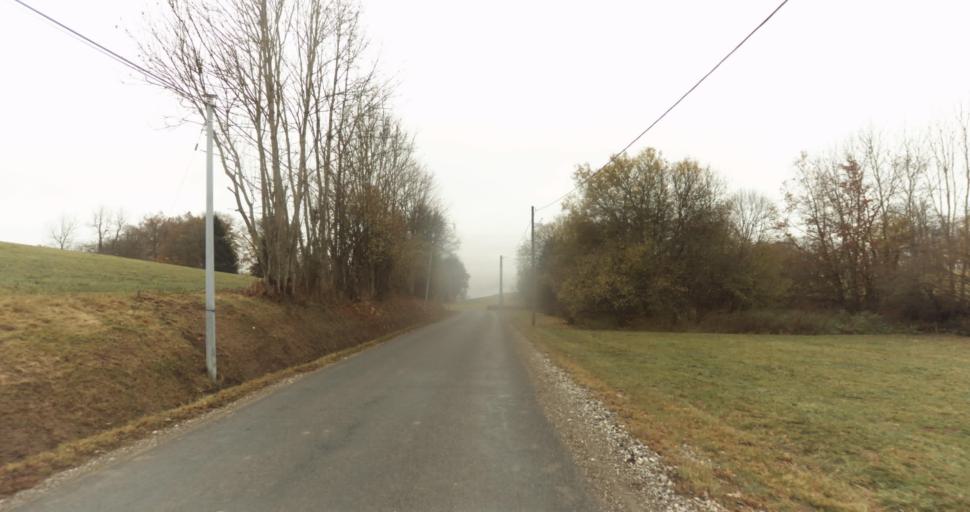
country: FR
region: Rhone-Alpes
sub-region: Departement de la Haute-Savoie
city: Evires
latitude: 46.0587
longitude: 6.2079
